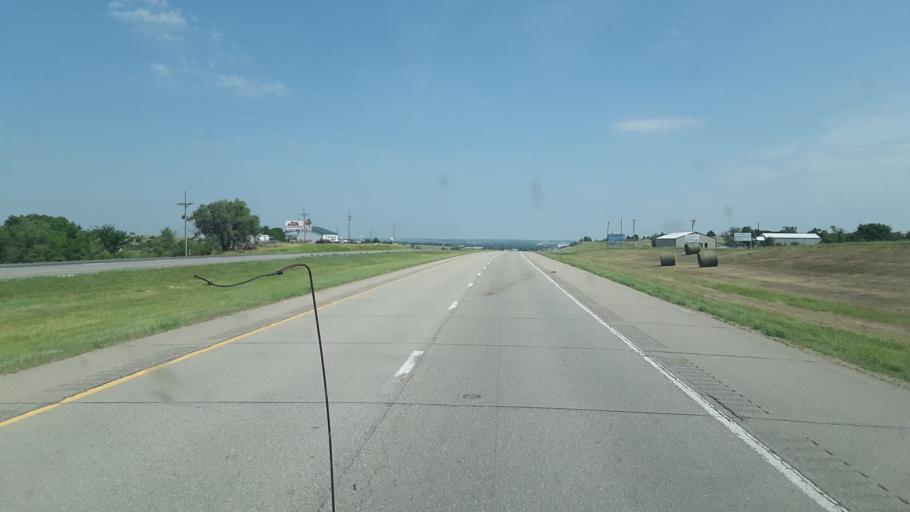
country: US
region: Kansas
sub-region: Cloud County
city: Concordia
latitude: 39.5301
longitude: -97.6570
